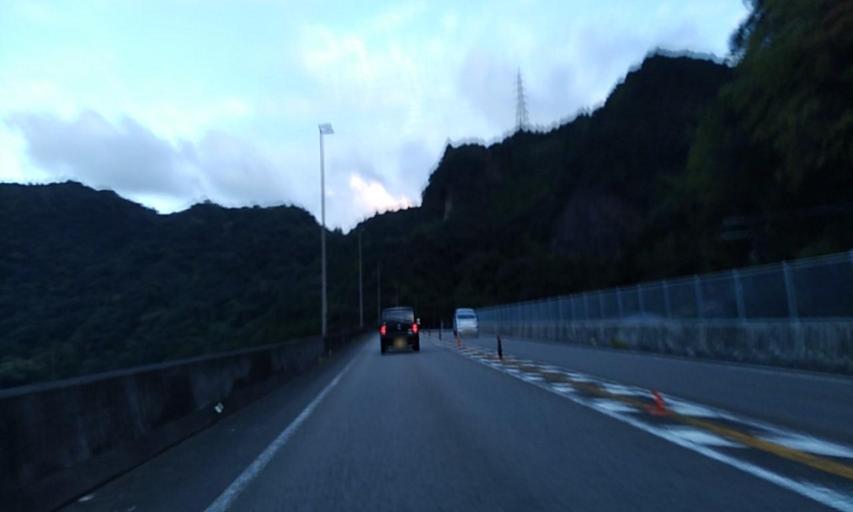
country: JP
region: Wakayama
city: Shingu
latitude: 33.7213
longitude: 135.9720
